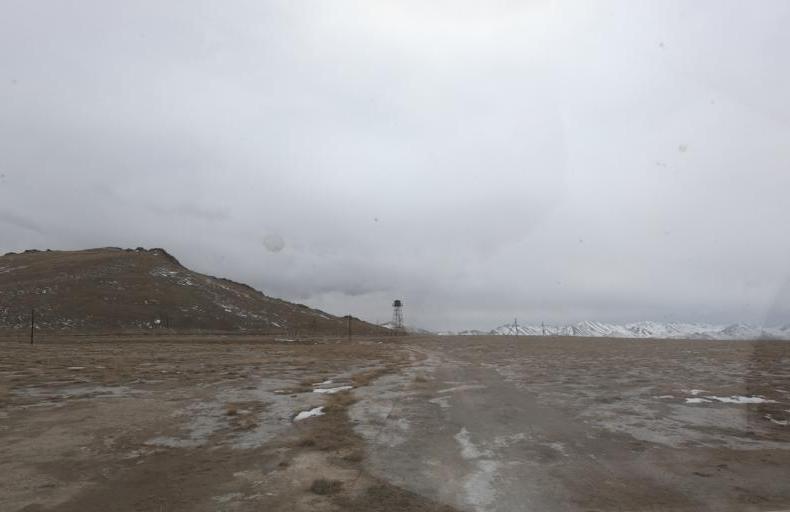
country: KG
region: Naryn
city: At-Bashi
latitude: 40.6459
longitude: 75.4313
